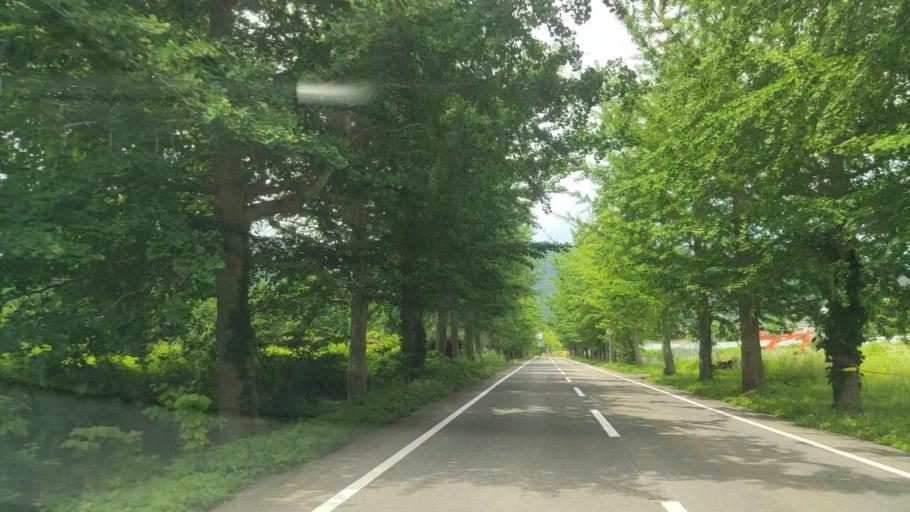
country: JP
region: Hyogo
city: Toyooka
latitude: 35.4997
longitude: 134.6781
